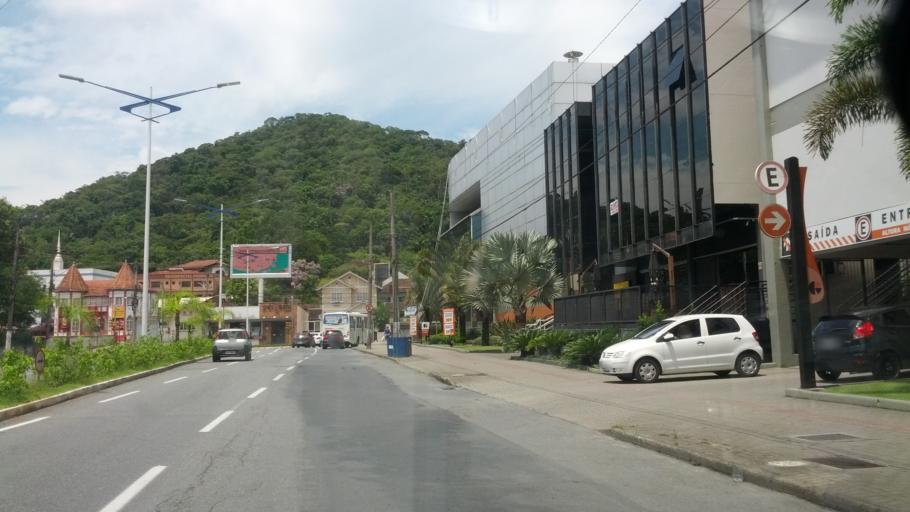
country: BR
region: Santa Catarina
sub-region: Blumenau
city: Blumenau
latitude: -26.9061
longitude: -49.0776
